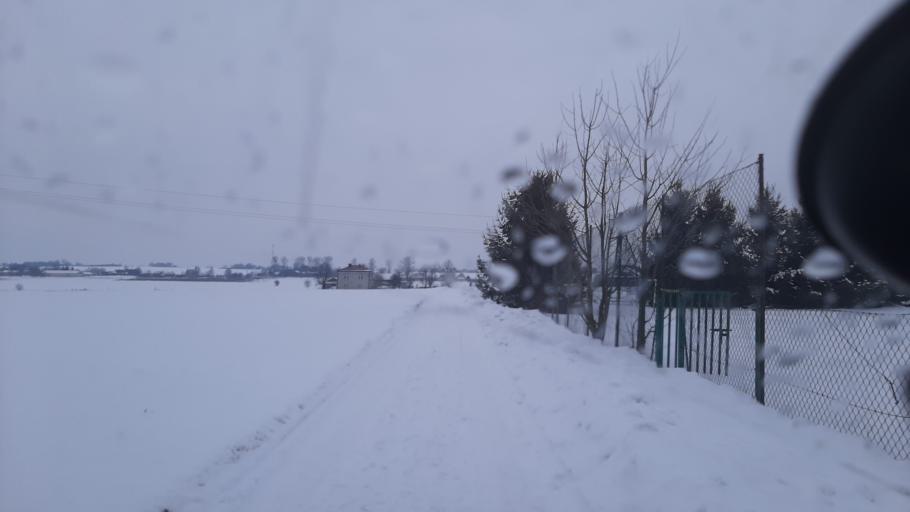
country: PL
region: Lublin Voivodeship
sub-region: Powiat lubelski
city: Jastkow
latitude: 51.3520
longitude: 22.4006
